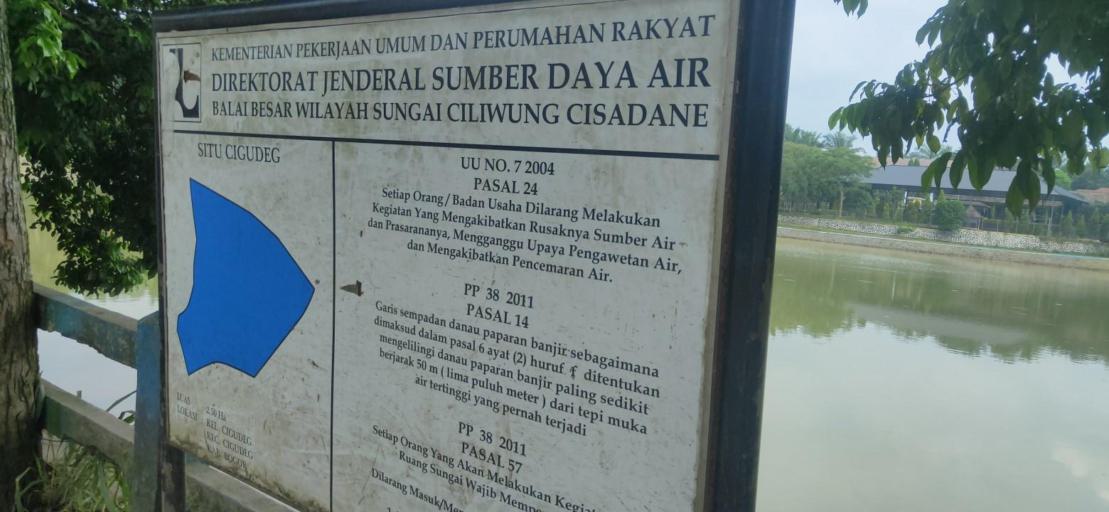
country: ID
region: West Java
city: Kompa Satu
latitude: -6.5523
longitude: 106.5367
